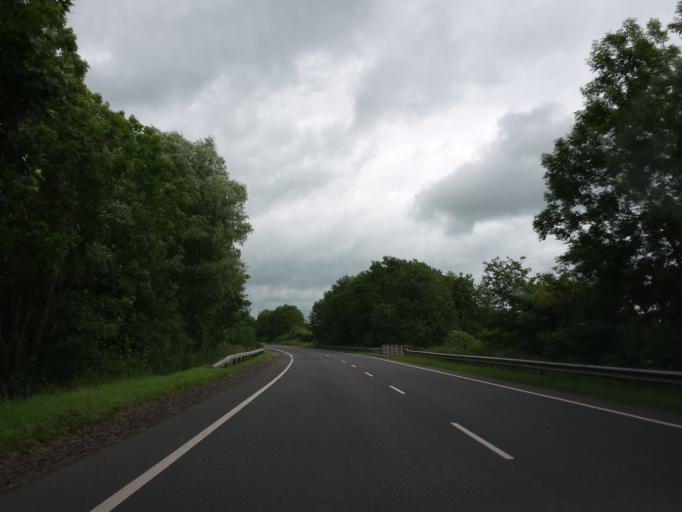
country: GB
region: Scotland
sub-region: Dumfries and Galloway
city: Castle Douglas
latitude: 54.9506
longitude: -3.9301
